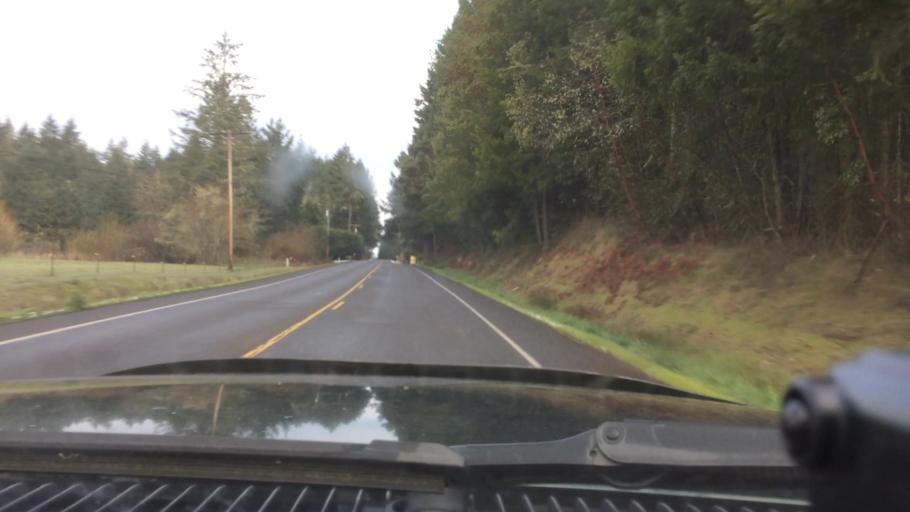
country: US
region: Oregon
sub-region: Lane County
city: Veneta
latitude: 44.1343
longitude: -123.3498
